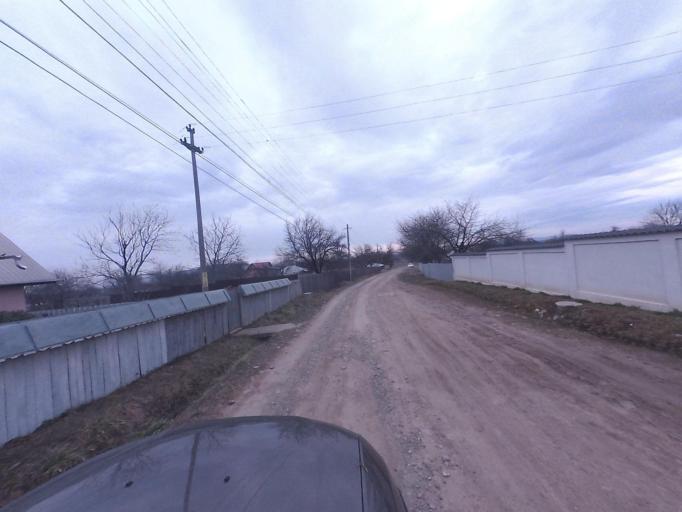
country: RO
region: Neamt
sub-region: Oras Targu Neamt
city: Humulesti
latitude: 47.1895
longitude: 26.3395
